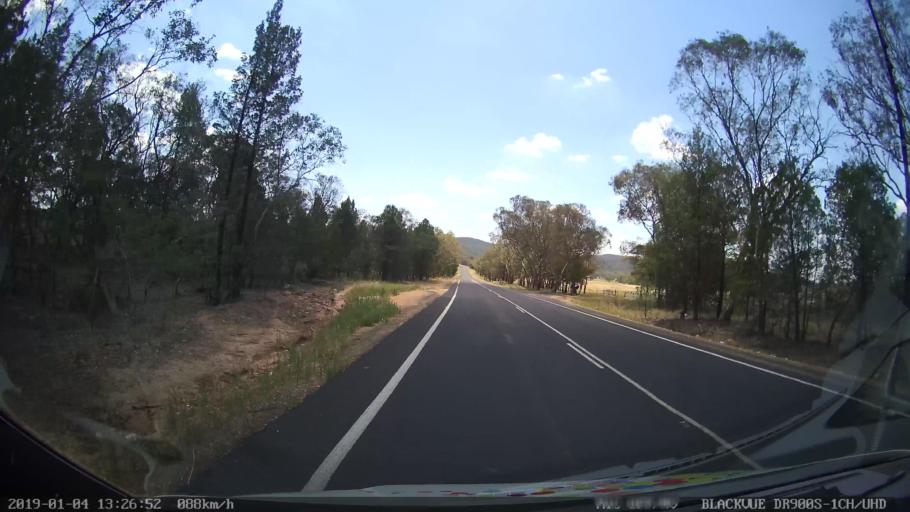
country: AU
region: New South Wales
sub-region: Parkes
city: Peak Hill
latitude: -32.6762
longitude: 148.5603
